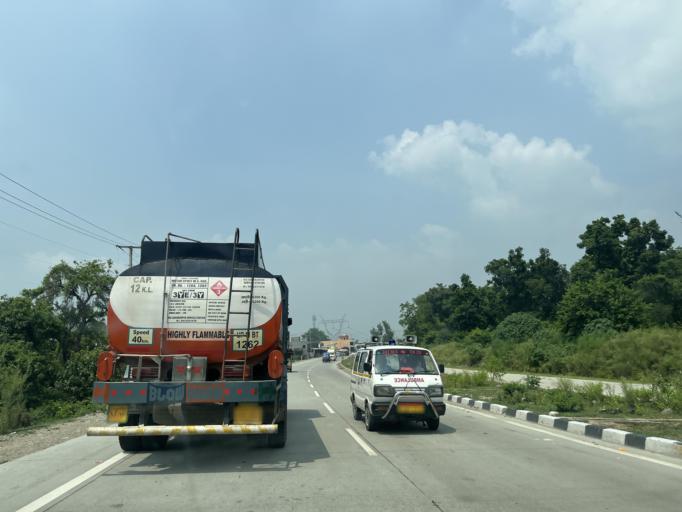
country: IN
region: Uttarakhand
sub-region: Haridwar
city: Haridwar
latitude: 29.8469
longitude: 78.1858
